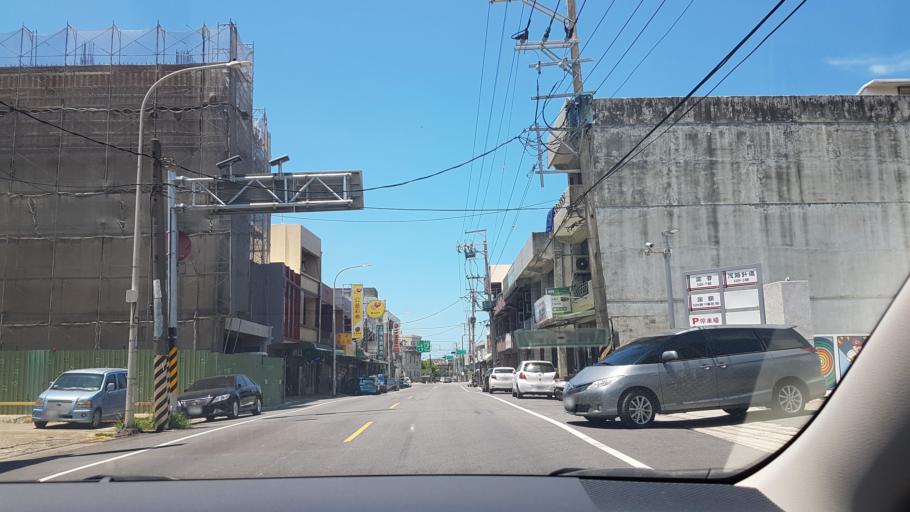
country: TW
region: Taiwan
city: Taoyuan City
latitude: 25.1106
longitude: 121.2548
